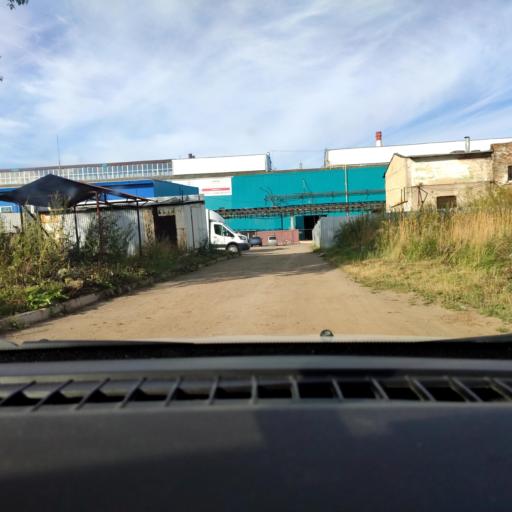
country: RU
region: Perm
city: Froly
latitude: 57.9619
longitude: 56.2780
